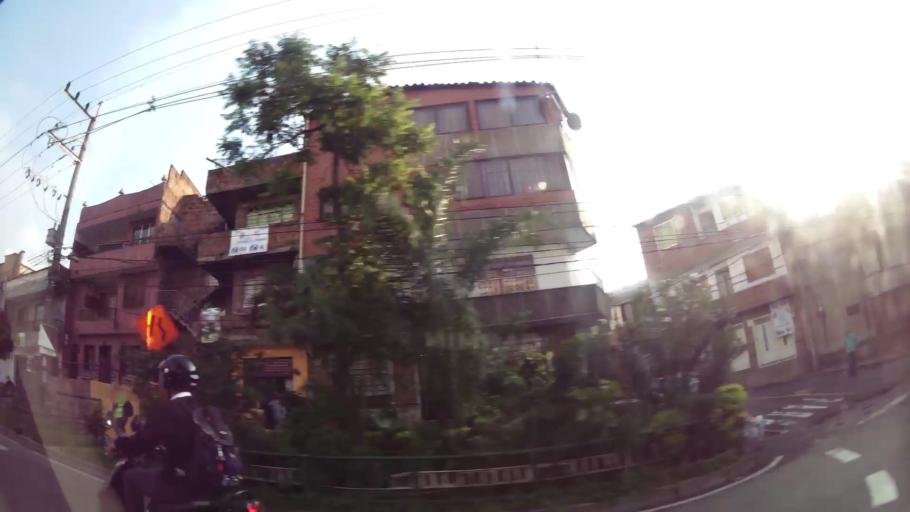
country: CO
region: Antioquia
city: Sabaneta
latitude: 6.1677
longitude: -75.6186
